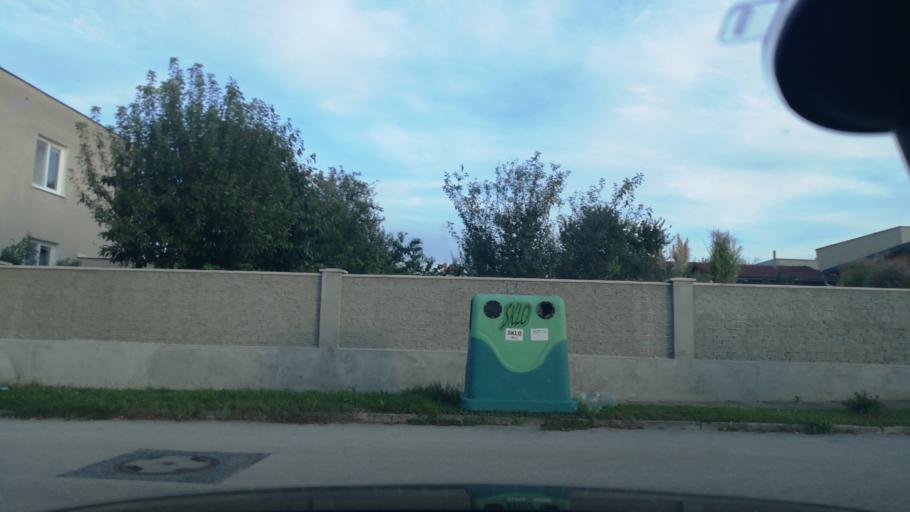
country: SK
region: Trnavsky
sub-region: Okres Skalica
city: Skalica
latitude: 48.8387
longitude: 17.2356
